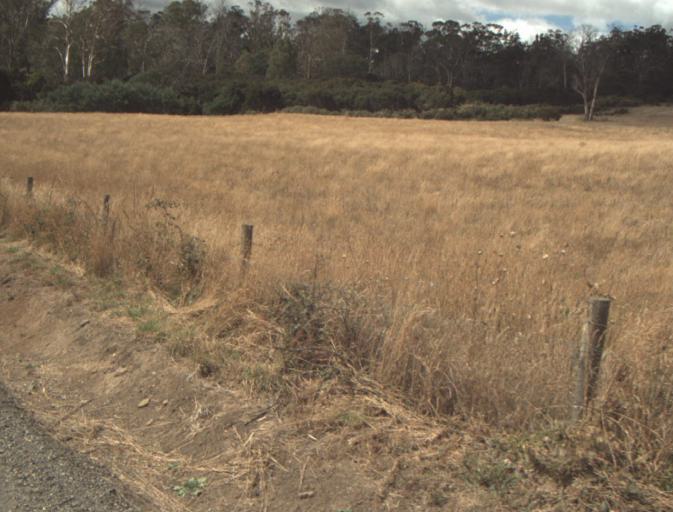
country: AU
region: Tasmania
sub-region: Launceston
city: Mayfield
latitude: -41.3046
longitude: 146.9953
